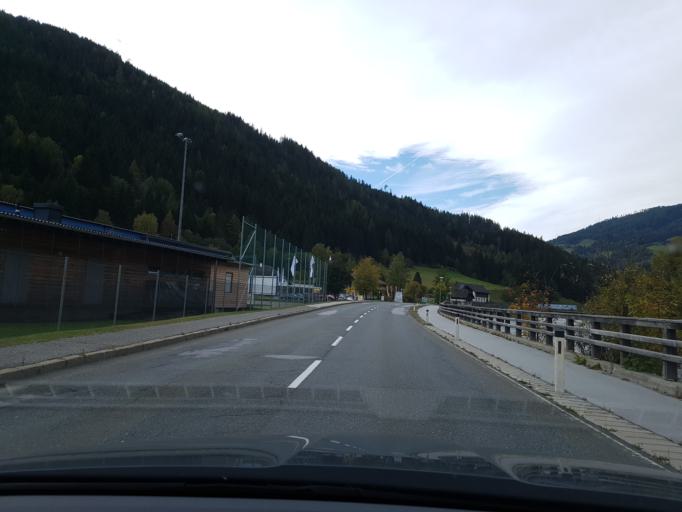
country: AT
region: Salzburg
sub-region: Politischer Bezirk Tamsweg
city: Ramingstein
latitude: 47.0748
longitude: 13.8325
